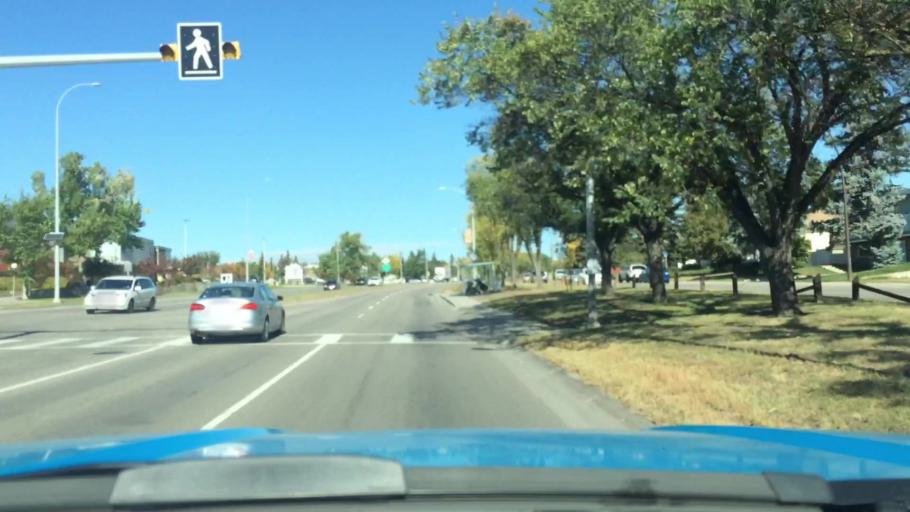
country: CA
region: Alberta
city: Calgary
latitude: 51.1157
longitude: -114.0672
